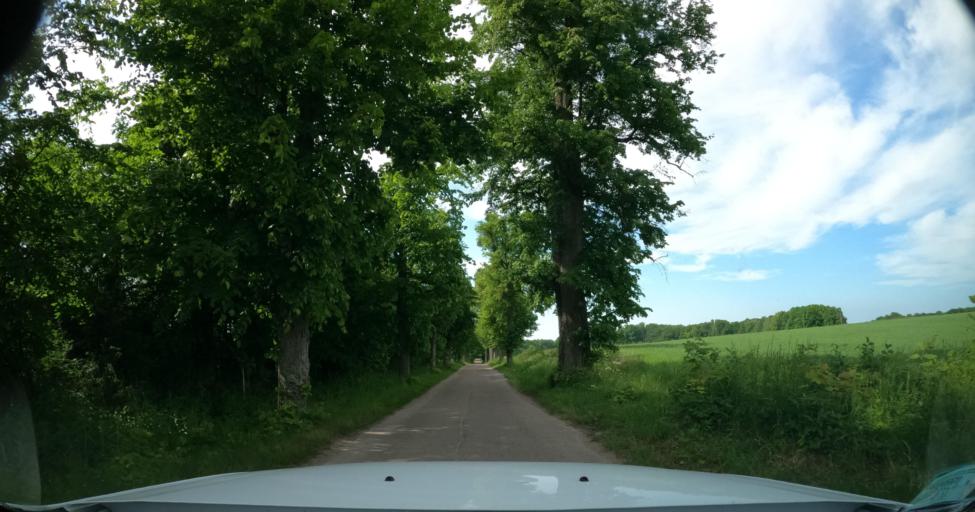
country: PL
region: Warmian-Masurian Voivodeship
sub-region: Powiat ostrodzki
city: Morag
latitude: 54.0210
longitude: 19.9140
